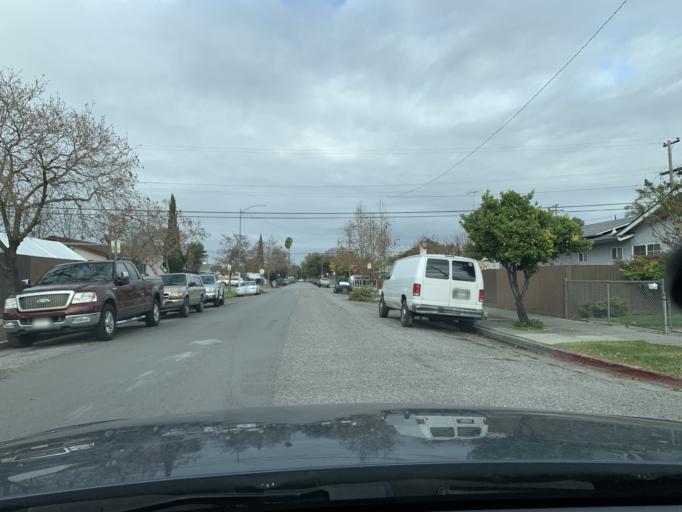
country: US
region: California
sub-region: Santa Clara County
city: Alum Rock
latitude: 37.3502
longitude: -121.8297
